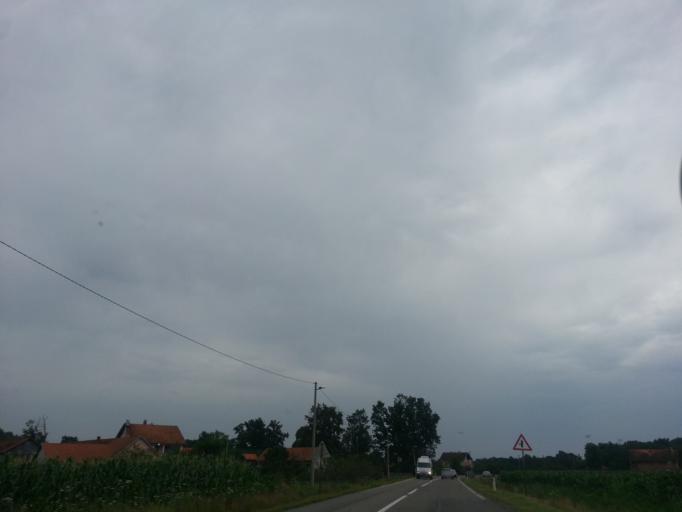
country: BA
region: Republika Srpska
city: Velika Obarska
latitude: 44.8221
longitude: 19.0463
